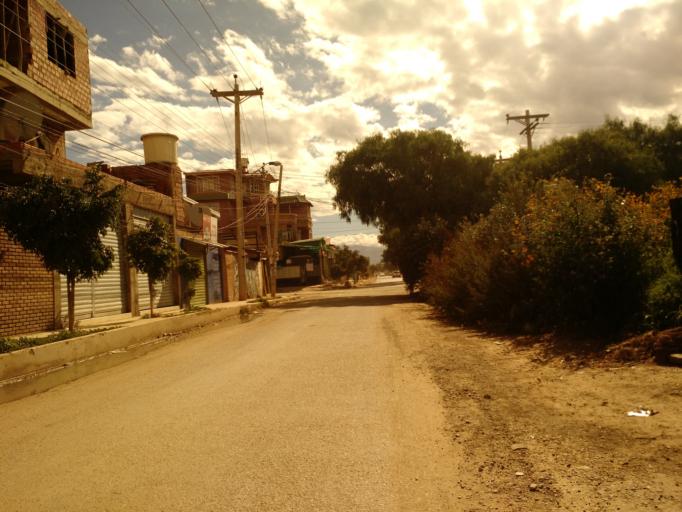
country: BO
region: Cochabamba
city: Cochabamba
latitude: -17.4572
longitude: -66.1565
